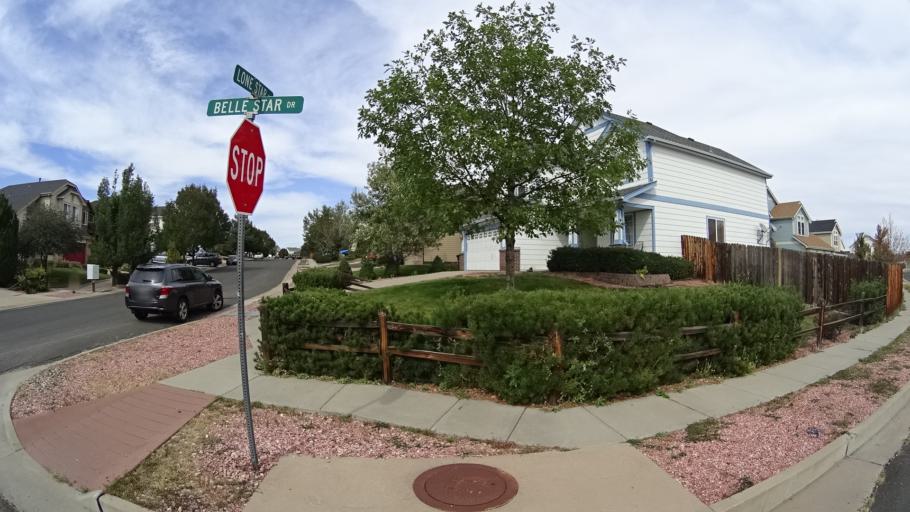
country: US
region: Colorado
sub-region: El Paso County
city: Cimarron Hills
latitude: 38.9062
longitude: -104.6986
